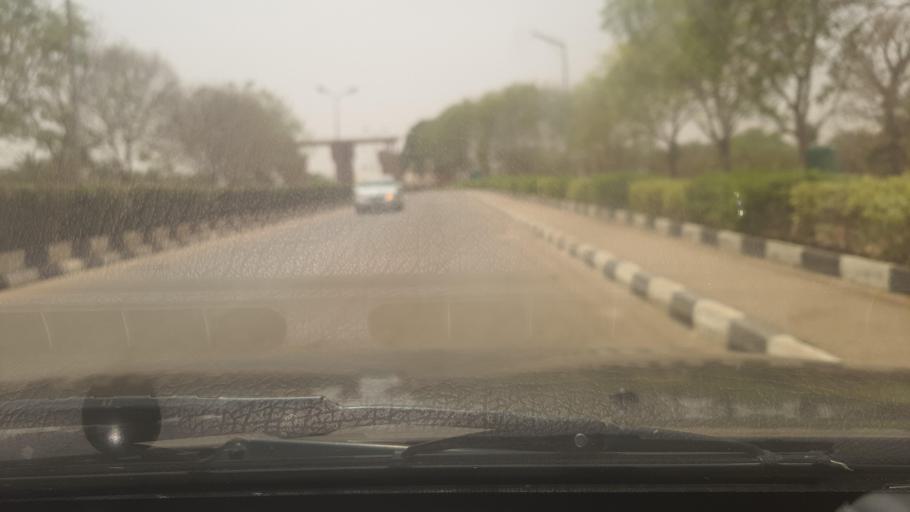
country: NG
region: Gombe
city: Gombe
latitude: 10.3038
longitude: 11.1720
